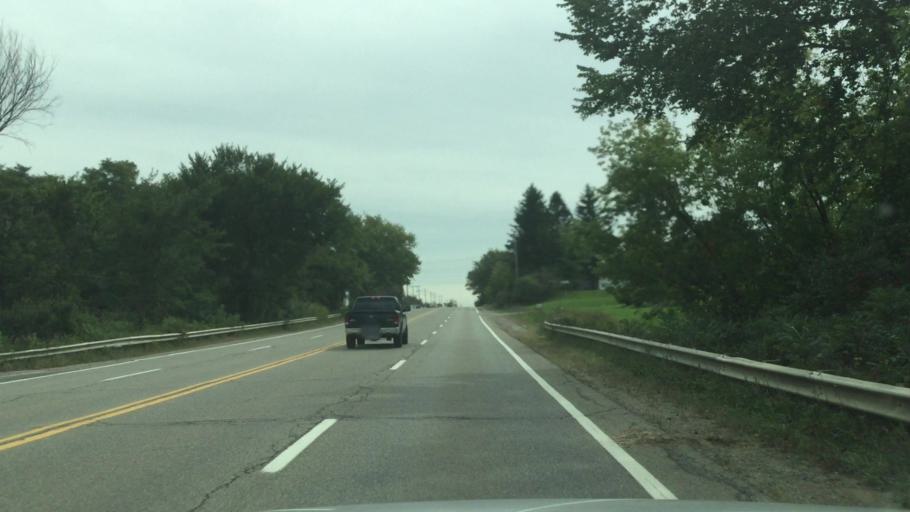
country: US
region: Michigan
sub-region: Oakland County
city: Ortonville
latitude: 42.7931
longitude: -83.5158
